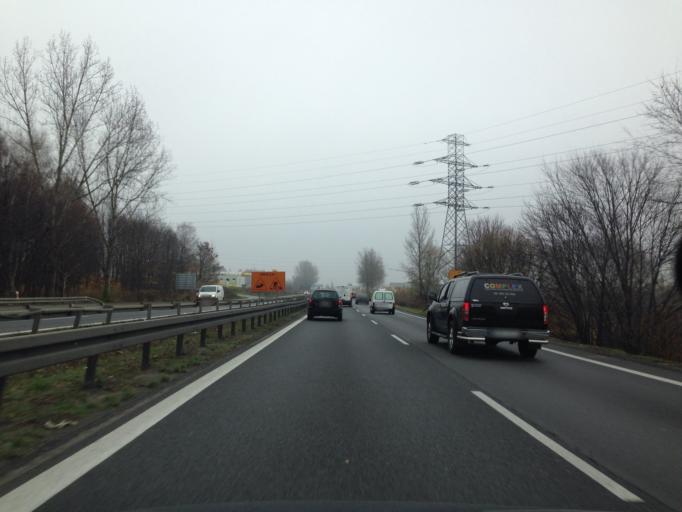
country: PL
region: Silesian Voivodeship
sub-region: Powiat bedzinski
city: Bedzin
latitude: 50.3075
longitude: 19.1144
